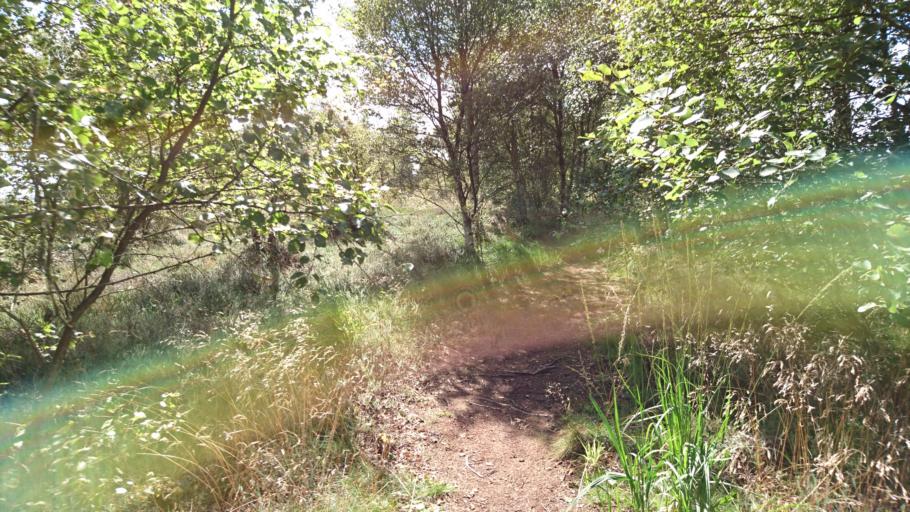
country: DK
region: North Denmark
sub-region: Alborg Kommune
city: Storvorde
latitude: 56.8674
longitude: 10.1753
